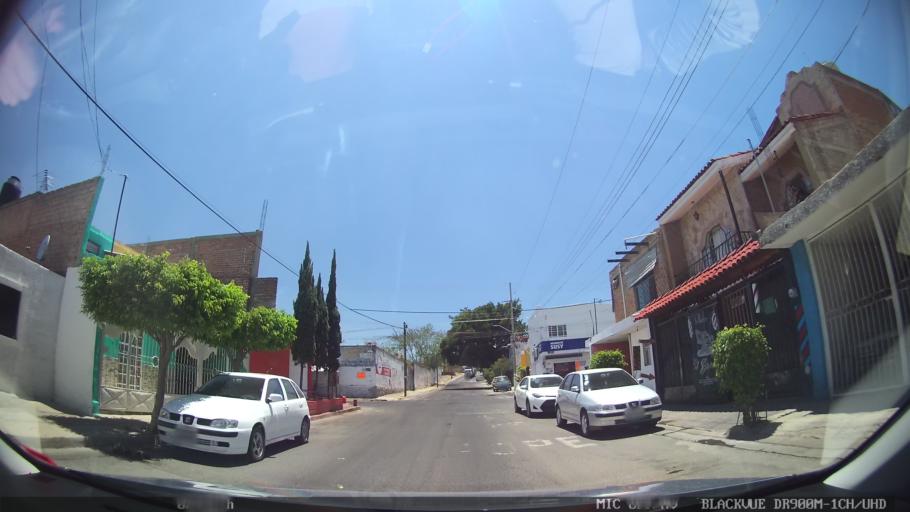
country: MX
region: Jalisco
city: Tlaquepaque
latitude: 20.6482
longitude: -103.2733
